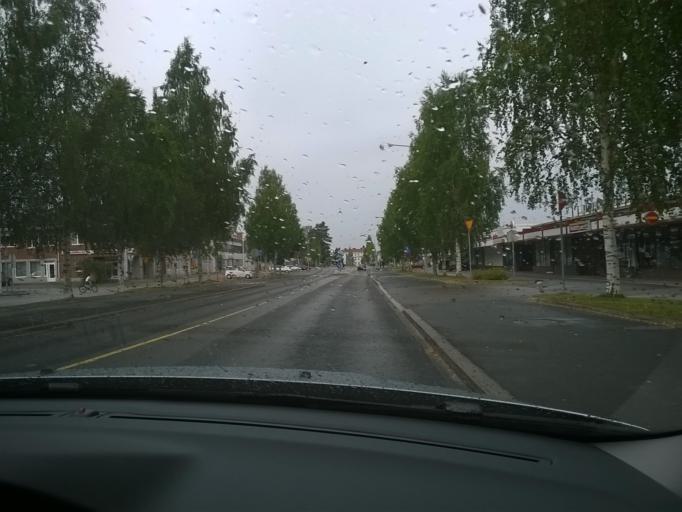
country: FI
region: Kainuu
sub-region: Kehys-Kainuu
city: Kuhmo
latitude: 64.1265
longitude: 29.5263
